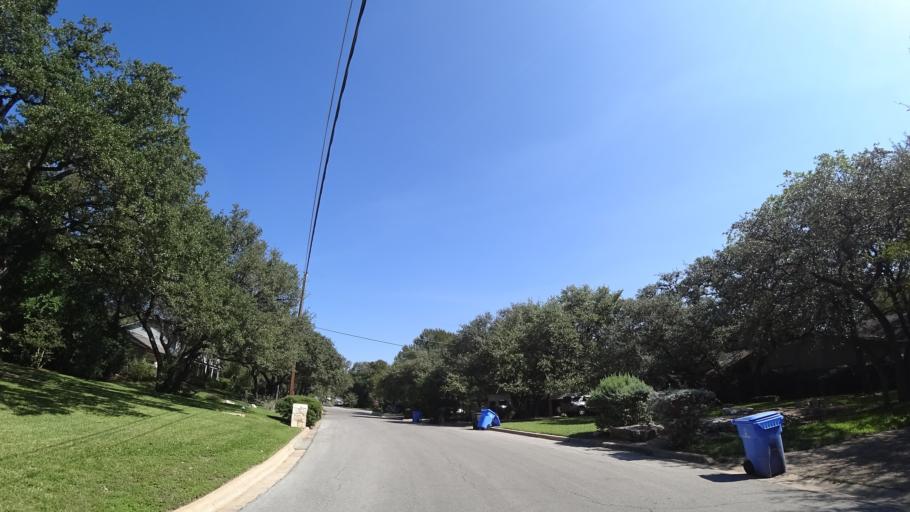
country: US
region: Texas
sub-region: Travis County
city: Rollingwood
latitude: 30.2698
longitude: -97.7823
